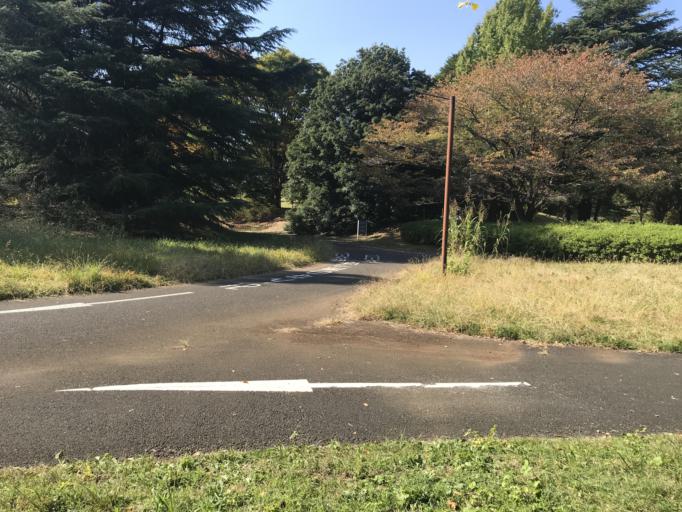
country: JP
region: Tokyo
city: Hino
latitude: 35.7139
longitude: 139.3986
